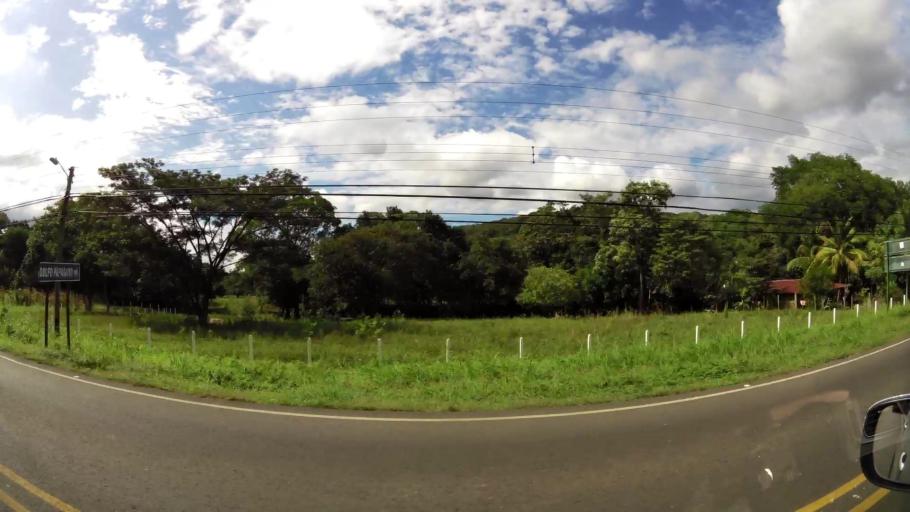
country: CR
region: Guanacaste
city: Hojancha
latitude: 10.1141
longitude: -85.3453
